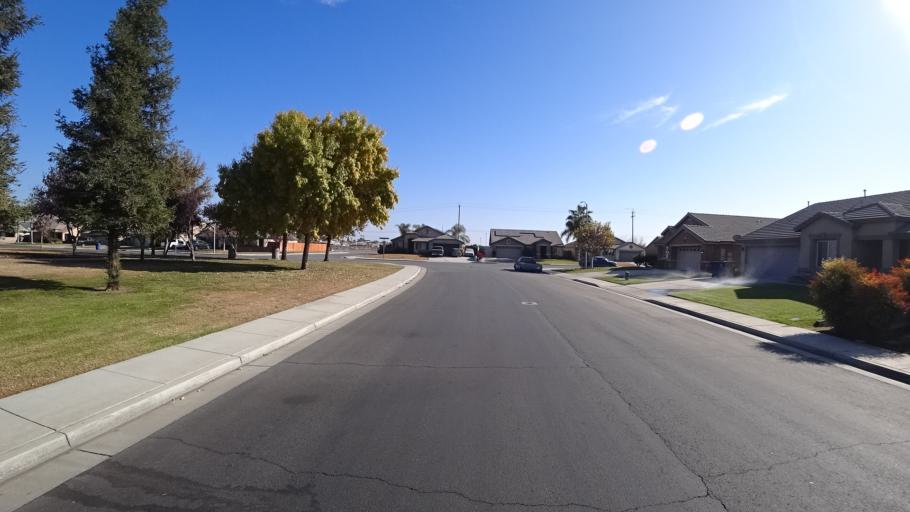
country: US
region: California
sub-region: Kern County
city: Greenfield
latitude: 35.2704
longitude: -119.0580
